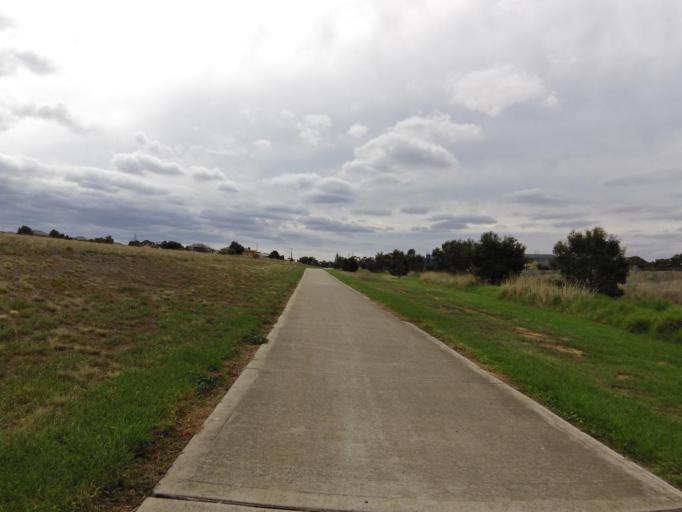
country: AU
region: Victoria
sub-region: Brimbank
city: Cairnlea
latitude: -37.7564
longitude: 144.7974
